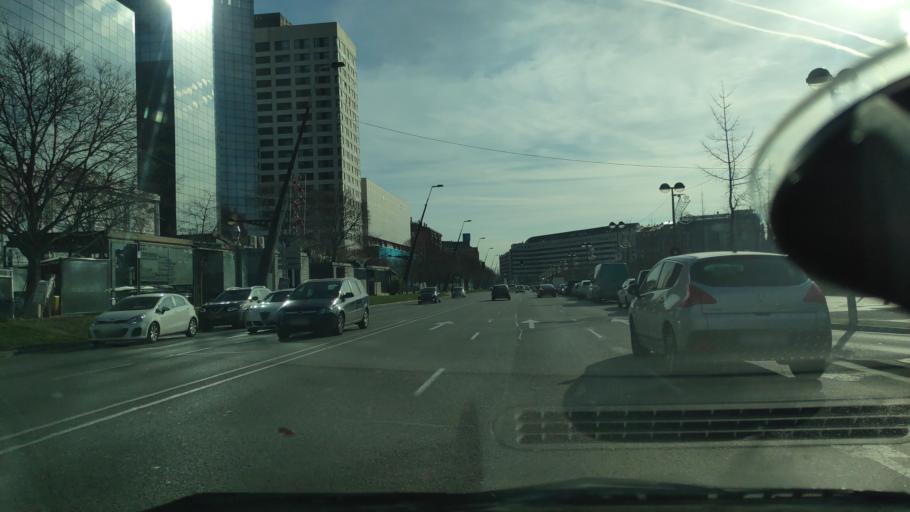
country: ES
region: Catalonia
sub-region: Provincia de Barcelona
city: Sabadell
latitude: 41.5535
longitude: 2.0977
